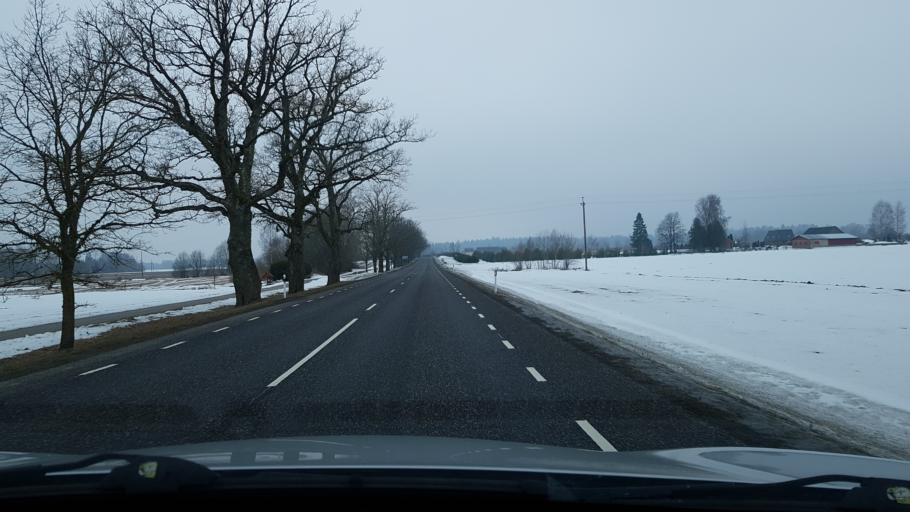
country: EE
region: Vorumaa
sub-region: Antsla vald
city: Vana-Antsla
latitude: 57.9132
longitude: 26.3019
